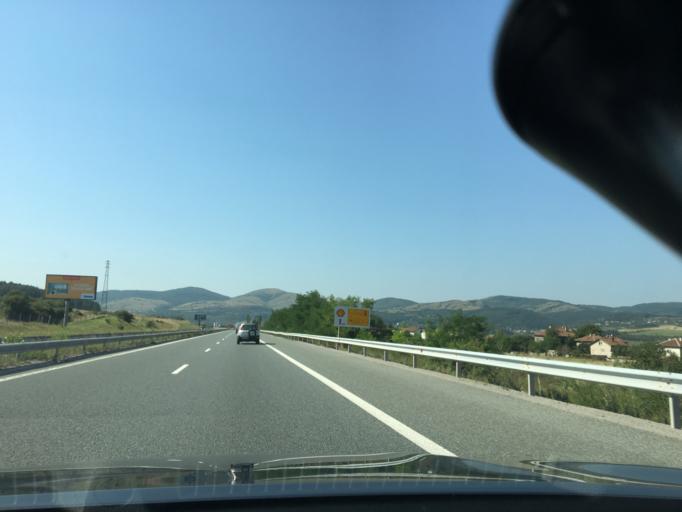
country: BG
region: Pernik
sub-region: Obshtina Pernik
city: Pernik
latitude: 42.5795
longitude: 23.1204
